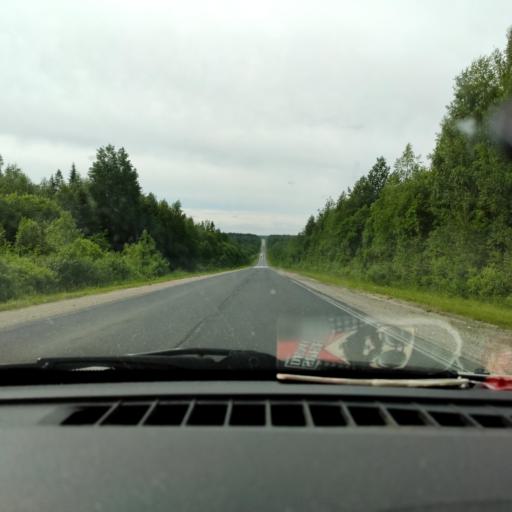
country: RU
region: Perm
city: Chusovoy
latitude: 58.3725
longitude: 57.9998
